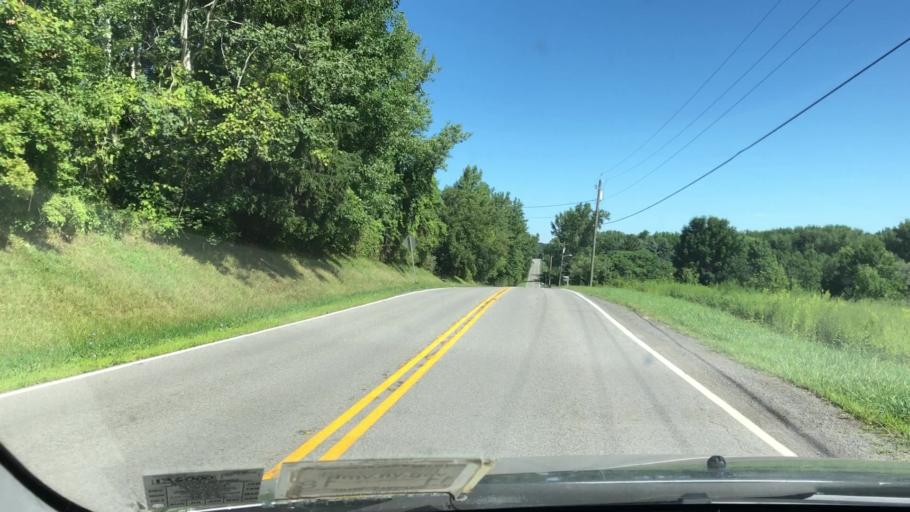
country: US
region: New York
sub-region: Monroe County
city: Fairport
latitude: 43.1102
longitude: -77.3730
